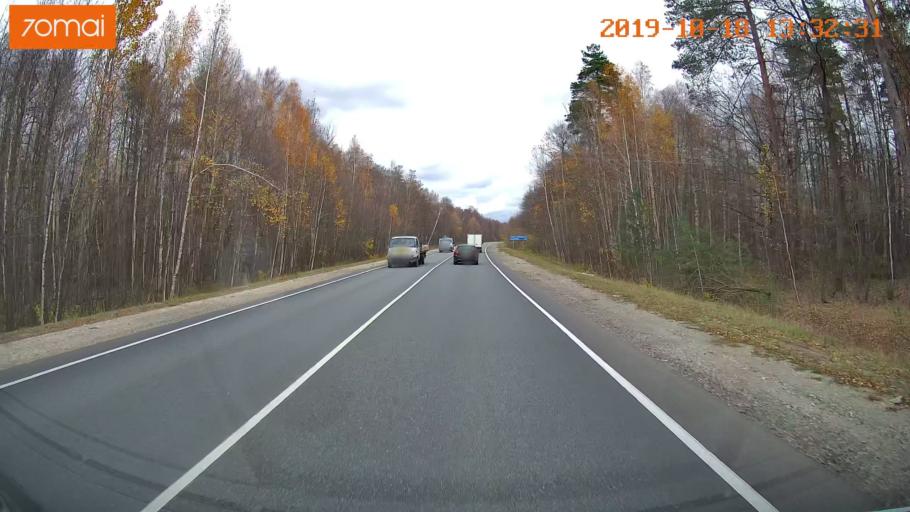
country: RU
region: Rjazan
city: Solotcha
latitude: 54.8343
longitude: 39.9197
